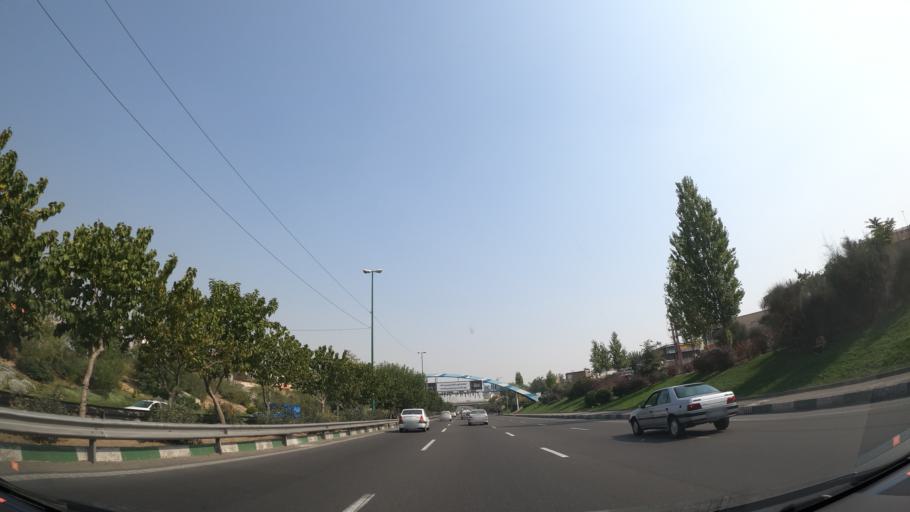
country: IR
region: Tehran
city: Tehran
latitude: 35.7539
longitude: 51.2754
